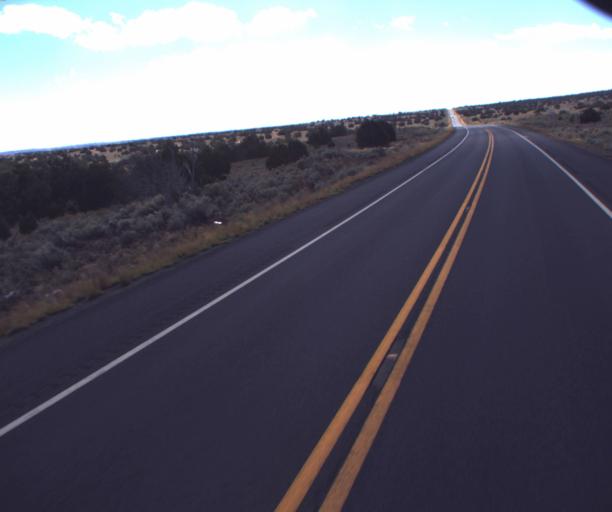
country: US
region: Arizona
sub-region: Apache County
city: Houck
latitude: 35.1688
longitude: -109.3383
